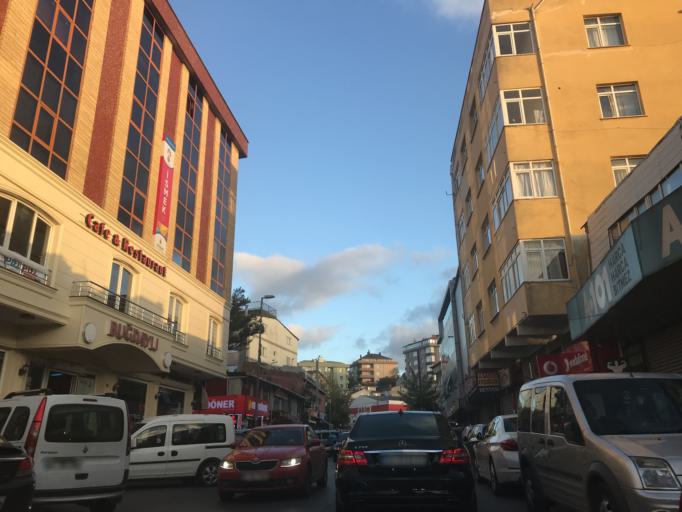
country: TR
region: Istanbul
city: Sisli
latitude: 41.1303
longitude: 29.0417
